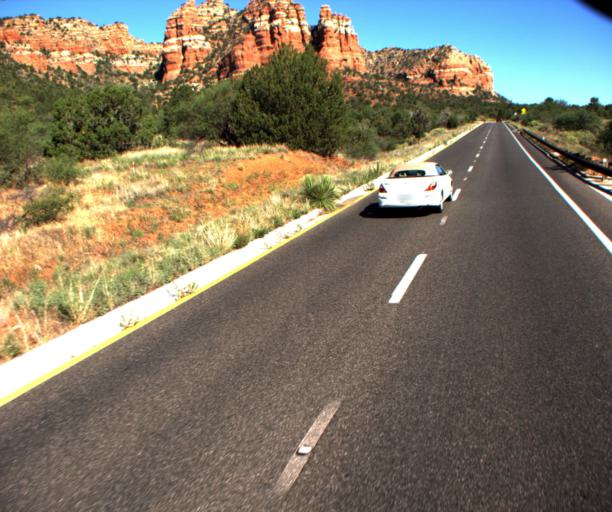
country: US
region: Arizona
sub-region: Yavapai County
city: Village of Oak Creek (Big Park)
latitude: 34.7971
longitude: -111.7659
